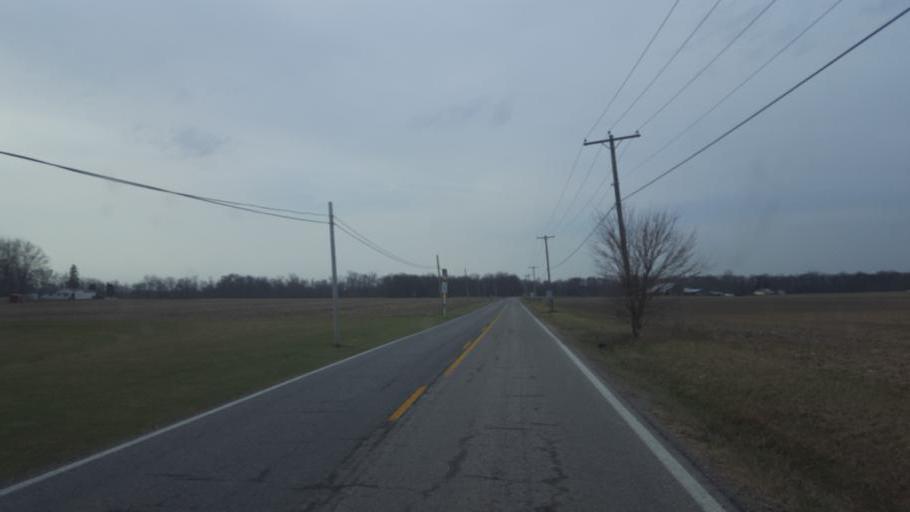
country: US
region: Ohio
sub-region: Morrow County
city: Cardington
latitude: 40.6262
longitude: -82.9674
